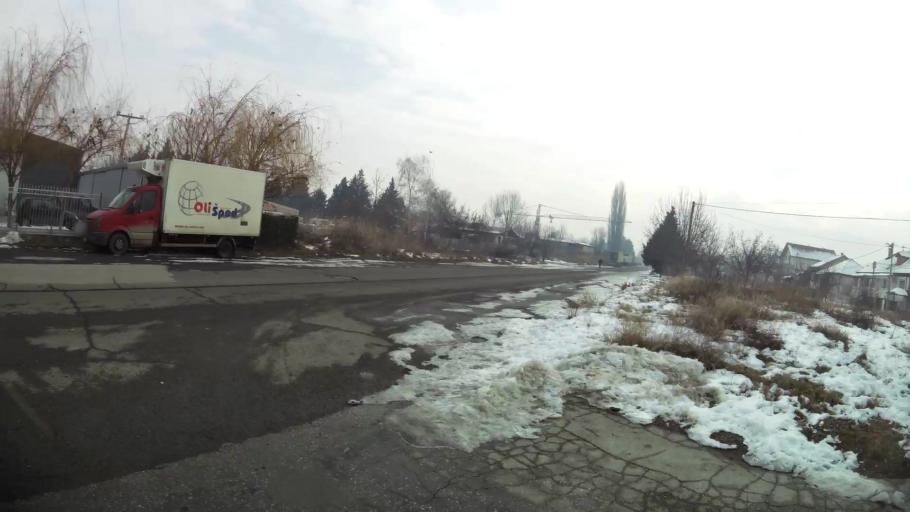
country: MK
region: Saraj
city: Saraj
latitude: 42.0211
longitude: 21.3584
